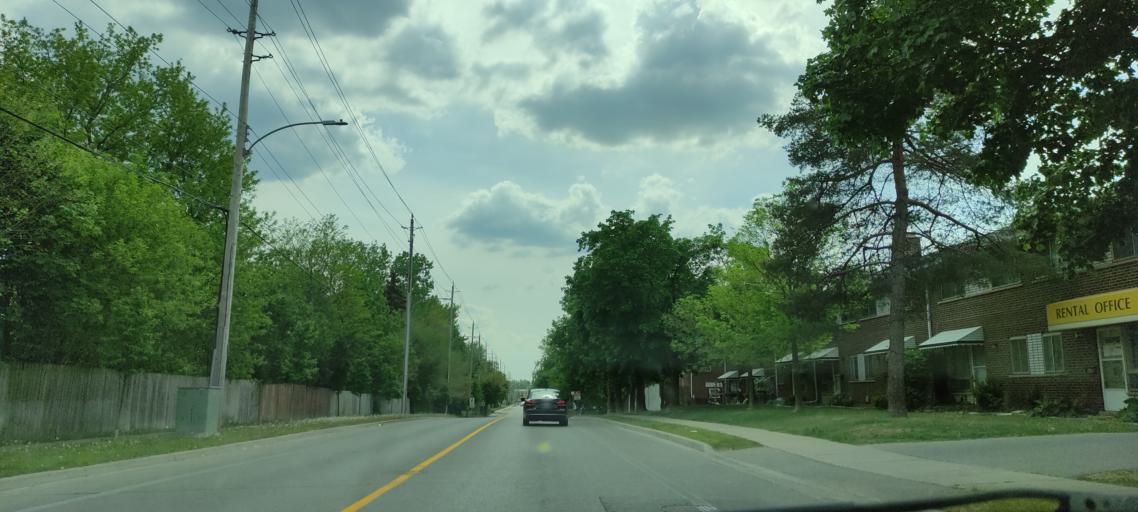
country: CA
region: Ontario
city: London
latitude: 43.0201
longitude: -81.2375
